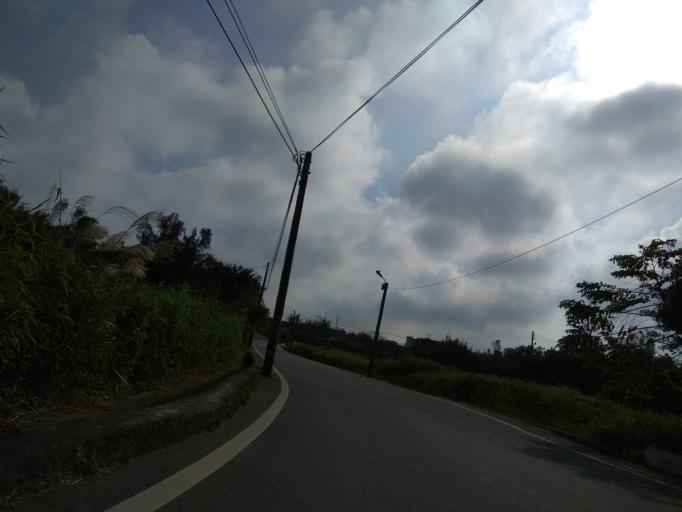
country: TW
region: Taiwan
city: Taoyuan City
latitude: 25.0646
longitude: 121.1551
